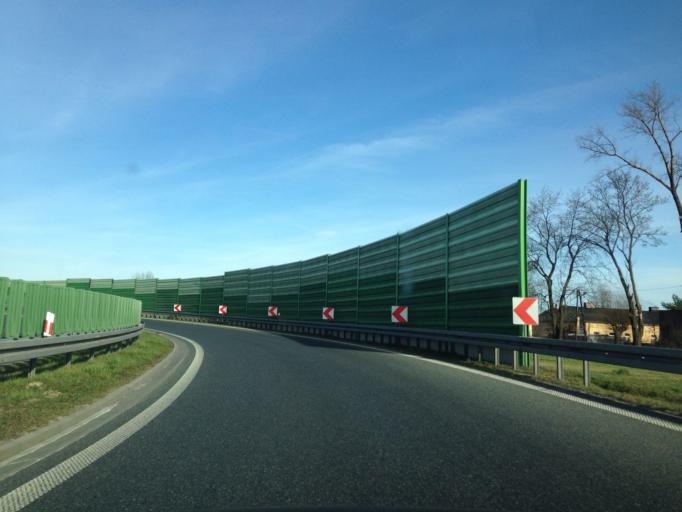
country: PL
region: Lodz Voivodeship
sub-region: Powiat kutnowski
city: Krosniewice
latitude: 52.2662
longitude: 19.1646
